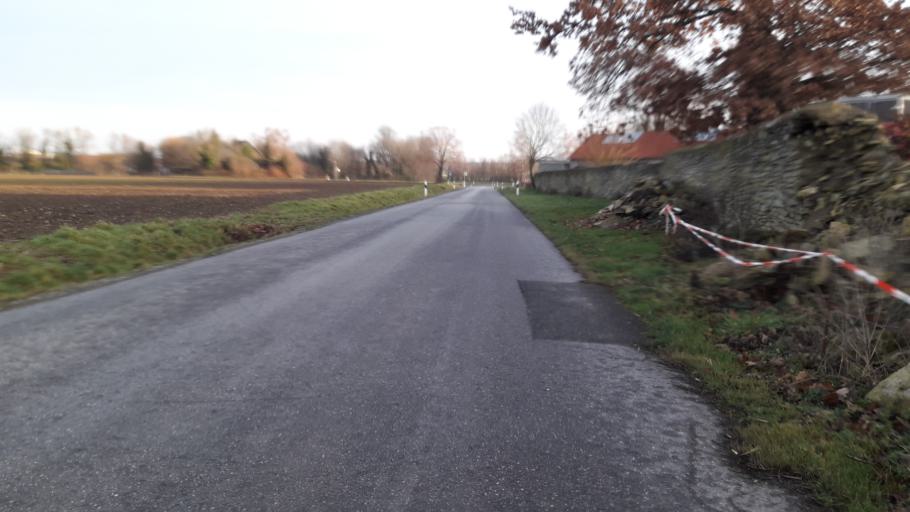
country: DE
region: North Rhine-Westphalia
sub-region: Regierungsbezirk Arnsberg
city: Soest
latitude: 51.5678
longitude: 8.0520
